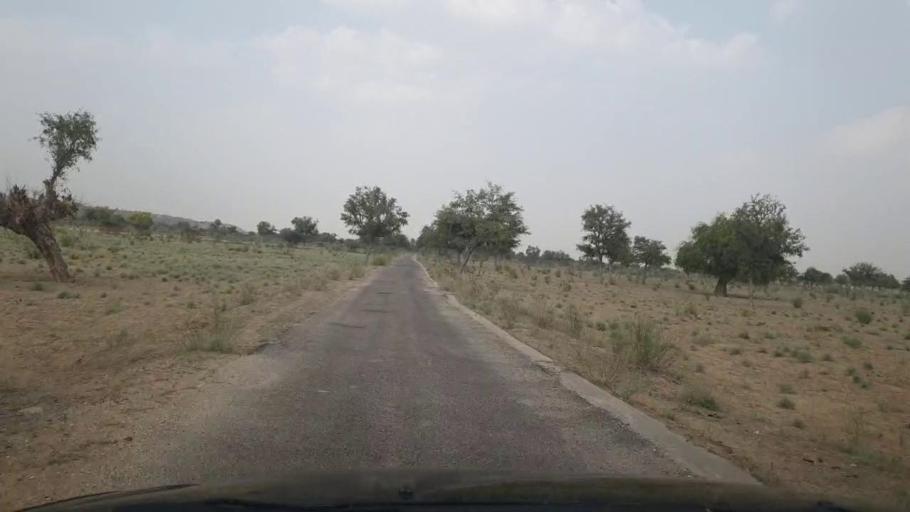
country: PK
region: Sindh
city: Islamkot
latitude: 24.9235
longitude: 70.5637
